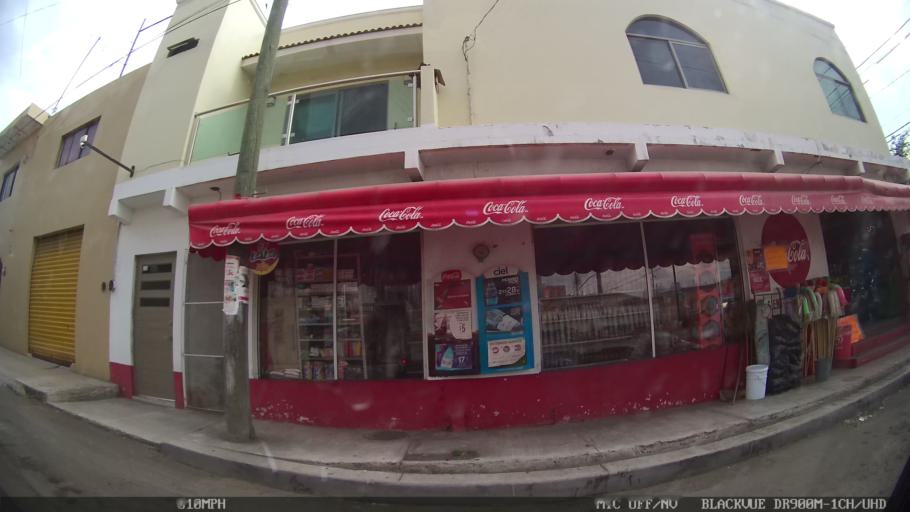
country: MX
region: Jalisco
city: Tonala
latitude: 20.6224
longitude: -103.2643
